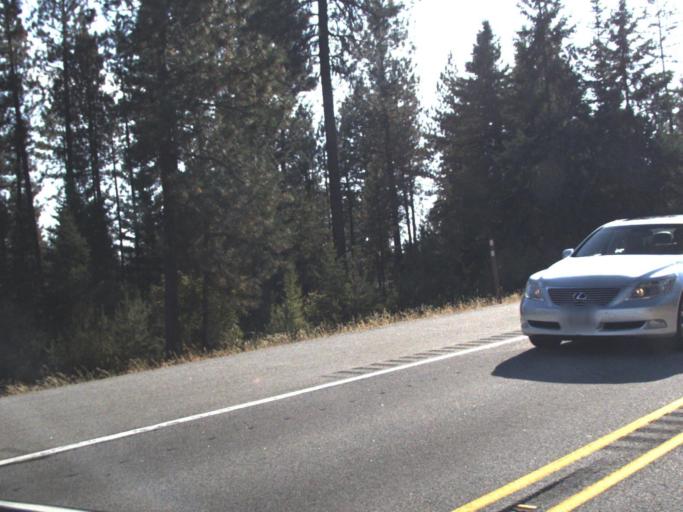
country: US
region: Washington
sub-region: Pend Oreille County
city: Newport
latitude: 48.1483
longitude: -117.1214
